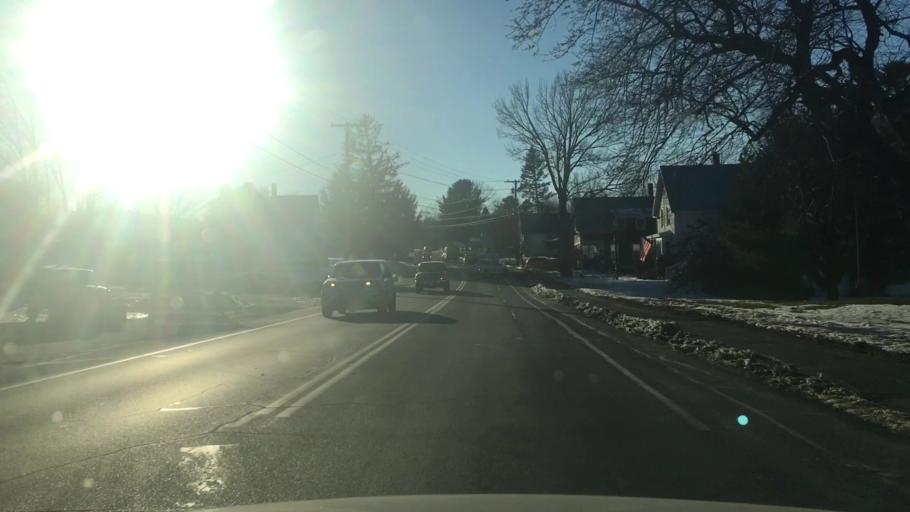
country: US
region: Maine
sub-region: Somerset County
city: Skowhegan
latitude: 44.7600
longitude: -69.7230
